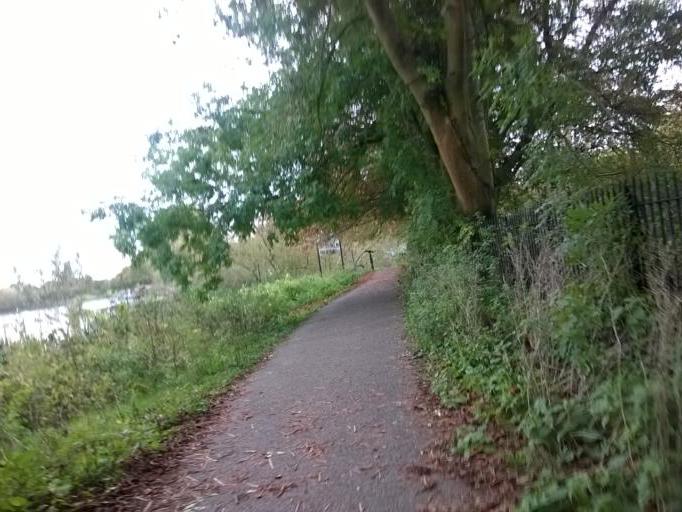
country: GB
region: England
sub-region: Reading
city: Reading
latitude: 51.4595
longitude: -0.9507
